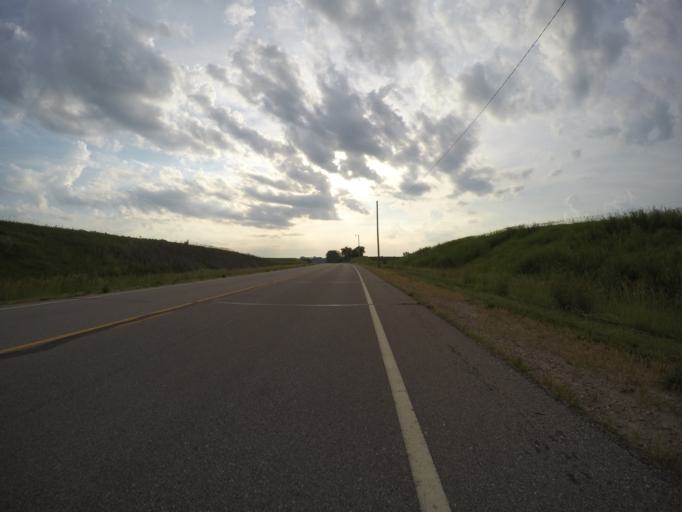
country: US
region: Kansas
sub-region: Doniphan County
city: Troy
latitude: 39.7901
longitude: -95.0824
